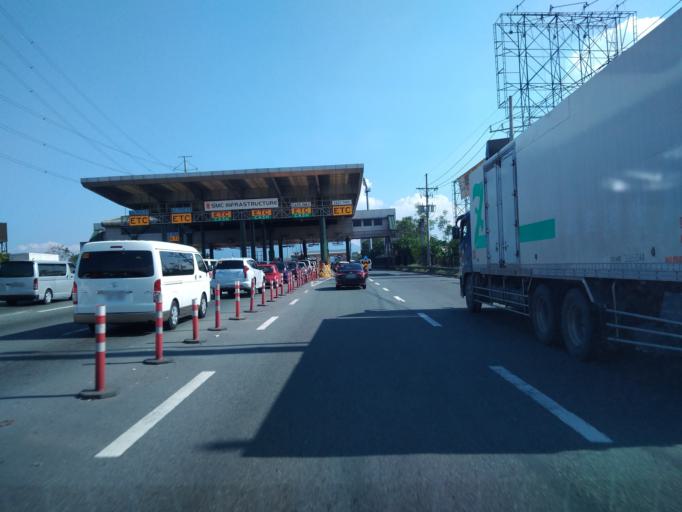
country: PH
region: Calabarzon
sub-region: Province of Laguna
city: Prinza
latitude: 14.2203
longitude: 121.1243
